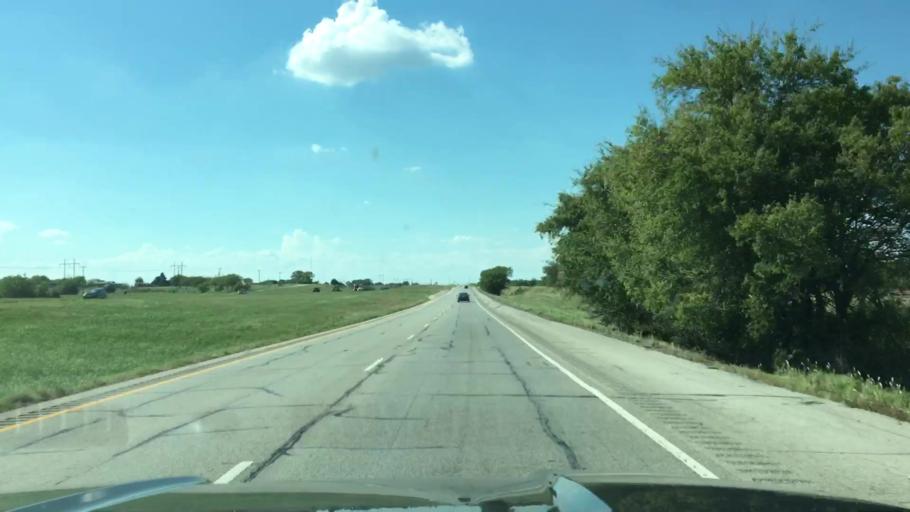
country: US
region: Texas
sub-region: Wise County
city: Boyd
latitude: 33.1600
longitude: -97.5236
